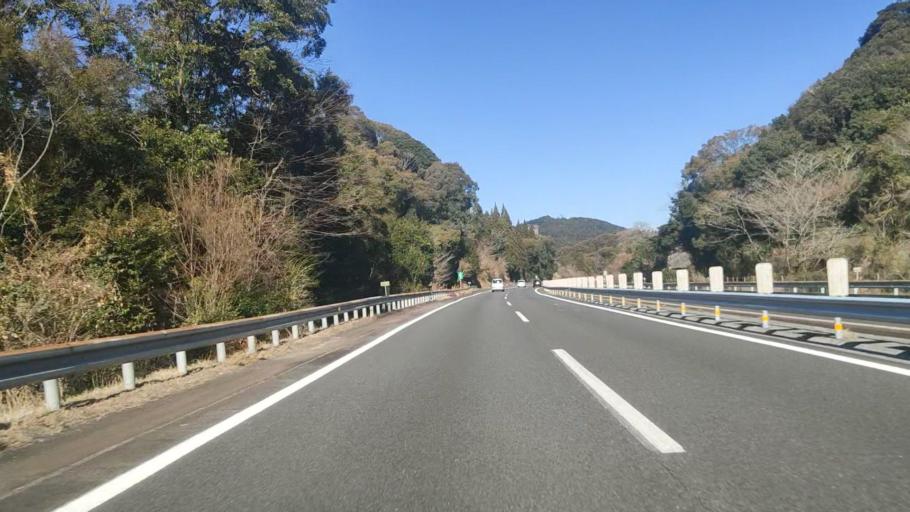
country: JP
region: Miyazaki
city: Miyakonojo
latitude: 31.8160
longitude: 131.2160
